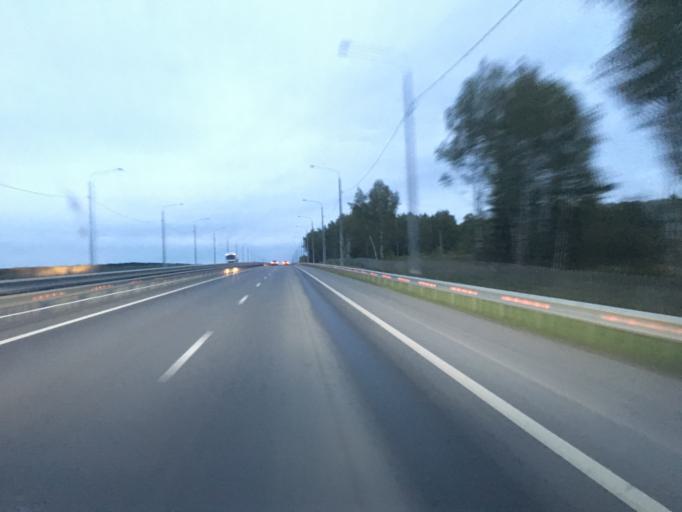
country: RU
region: Kaluga
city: Maloyaroslavets
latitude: 54.9425
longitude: 36.4333
